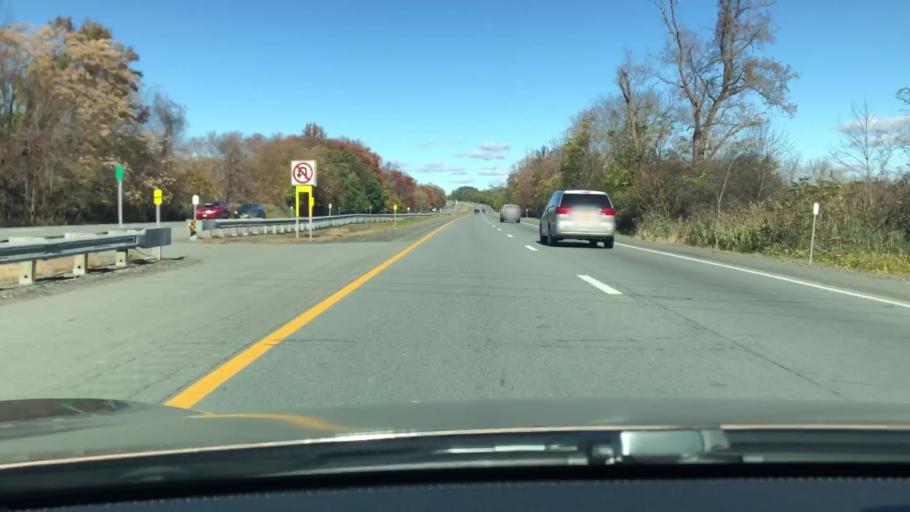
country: US
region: New York
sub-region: Orange County
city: Vails Gate
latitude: 41.4443
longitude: -74.0663
